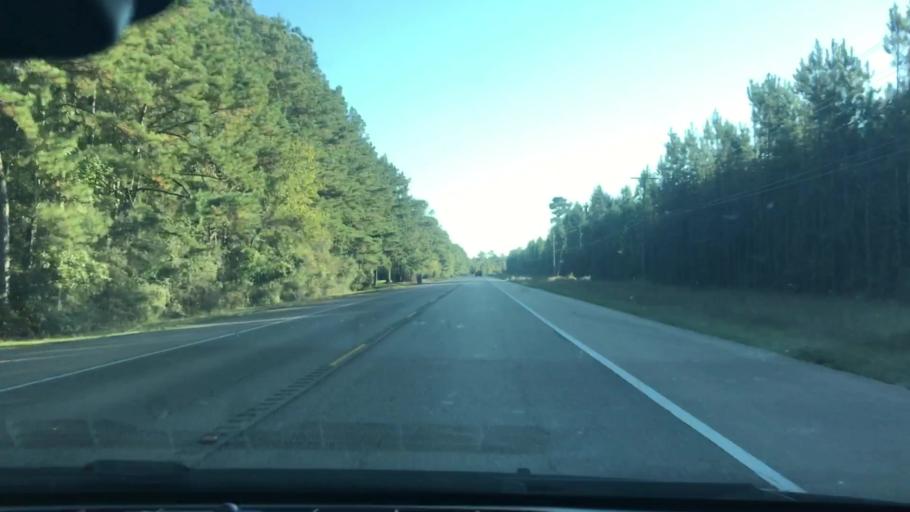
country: US
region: Louisiana
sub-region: Saint Tammany Parish
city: Abita Springs
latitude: 30.5663
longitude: -89.8715
